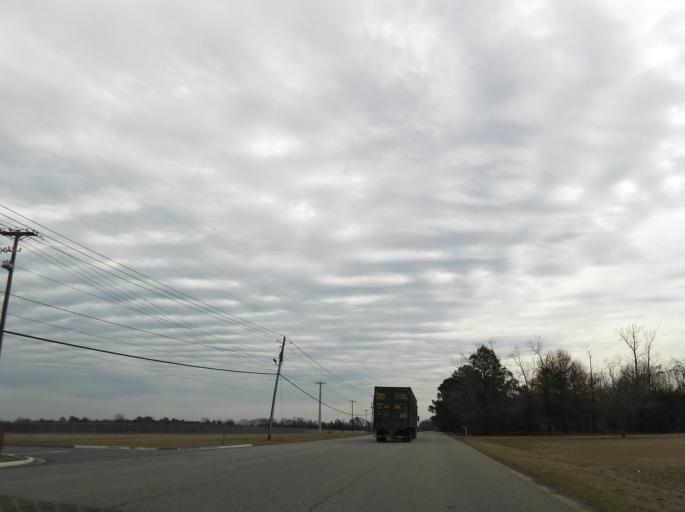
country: US
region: Georgia
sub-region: Houston County
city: Centerville
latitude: 32.6834
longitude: -83.6398
